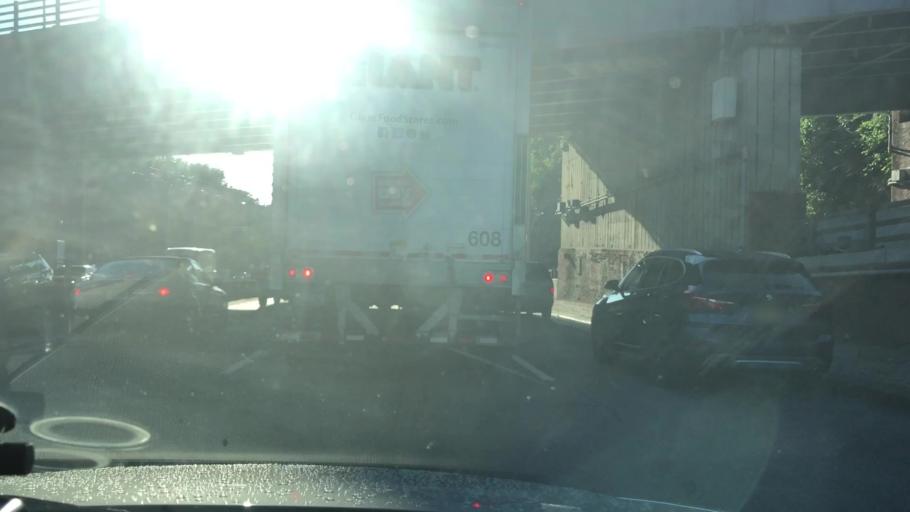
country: US
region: New York
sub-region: New York County
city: Inwood
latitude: 40.8444
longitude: -73.9205
